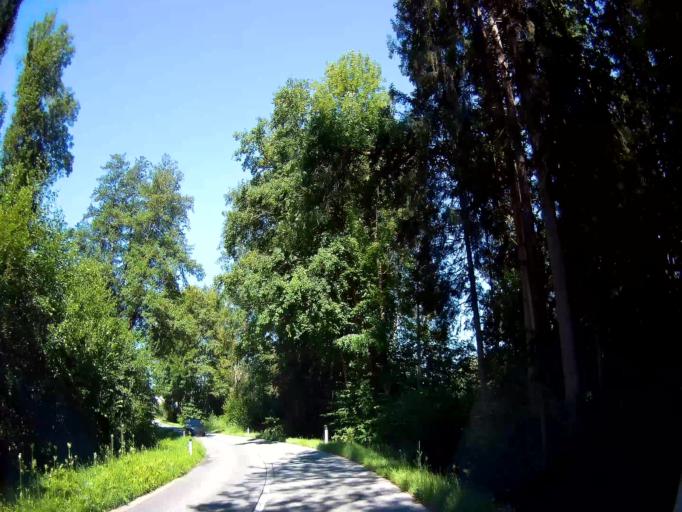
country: AT
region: Carinthia
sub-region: Politischer Bezirk Klagenfurt Land
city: Ebenthal
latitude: 46.6035
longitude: 14.4150
